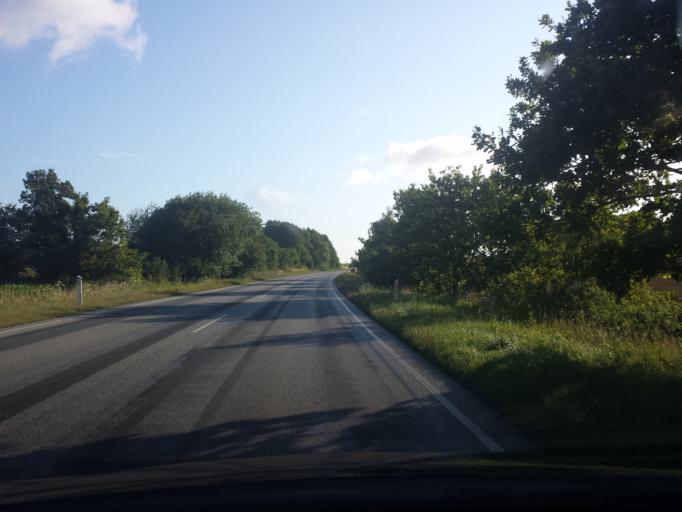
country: DK
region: South Denmark
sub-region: Sonderborg Kommune
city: Dybbol
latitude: 54.9165
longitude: 9.7109
